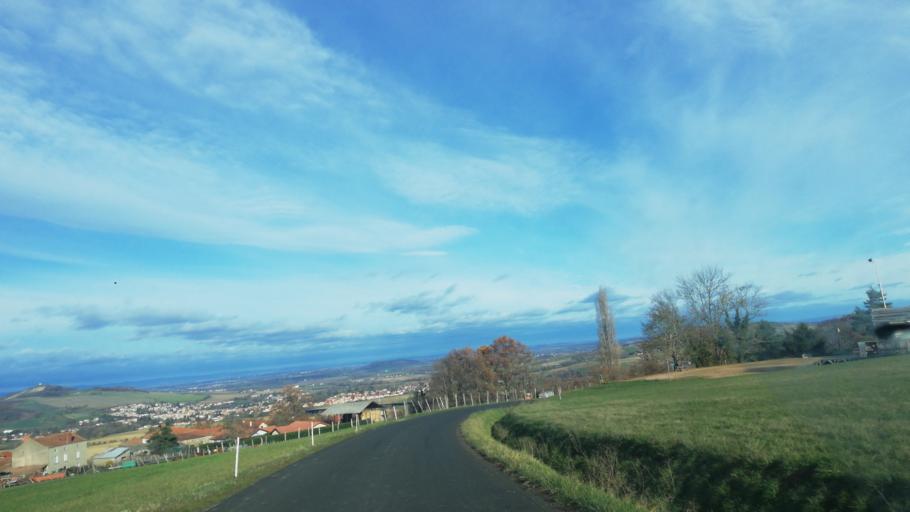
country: FR
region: Auvergne
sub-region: Departement du Puy-de-Dome
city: Billom
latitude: 45.6979
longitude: 3.3564
